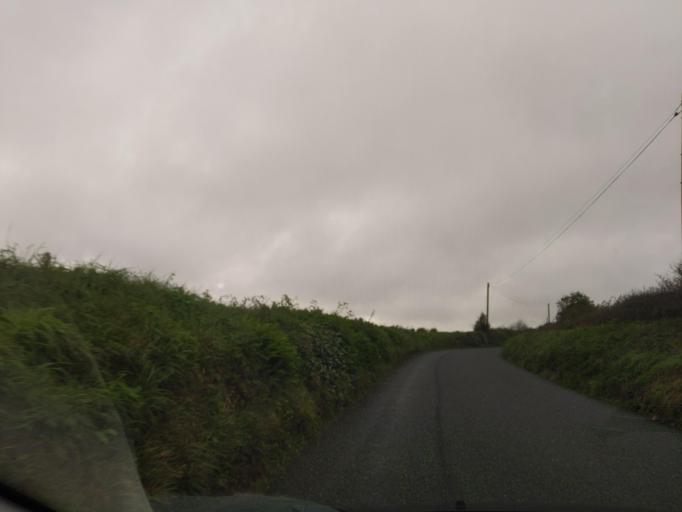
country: GB
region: England
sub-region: Cornwall
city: Saltash
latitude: 50.4498
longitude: -4.2362
